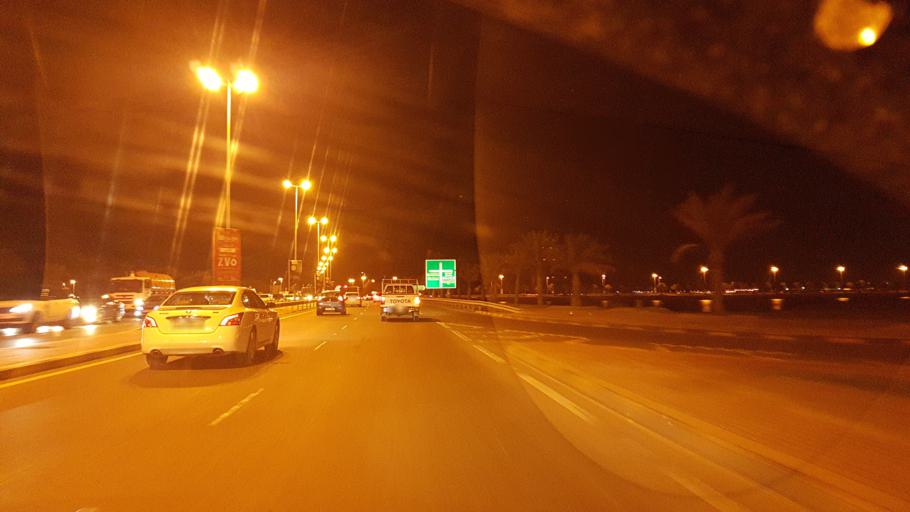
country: BH
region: Muharraq
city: Al Hadd
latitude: 26.2548
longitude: 50.6554
